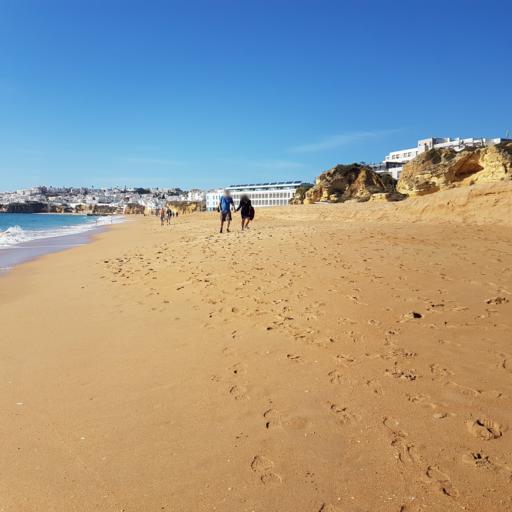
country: PT
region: Faro
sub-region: Albufeira
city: Albufeira
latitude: 37.0844
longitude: -8.2402
